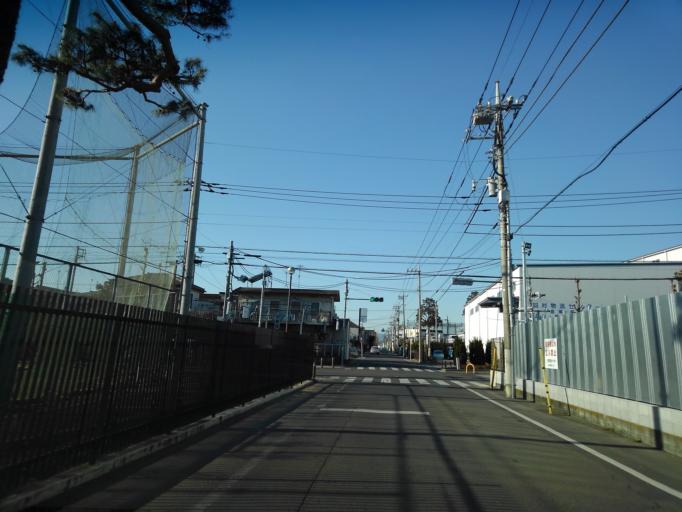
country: JP
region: Tokyo
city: Fussa
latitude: 35.7699
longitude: 139.3305
